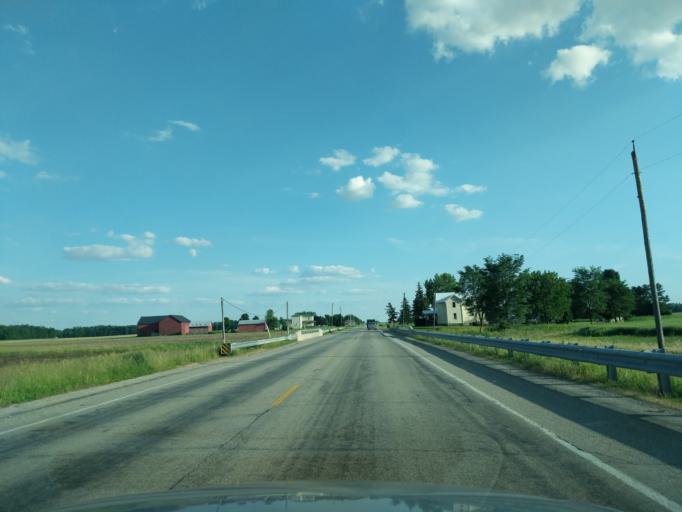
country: US
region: Indiana
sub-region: Whitley County
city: Columbia City
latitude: 41.0564
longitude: -85.4705
